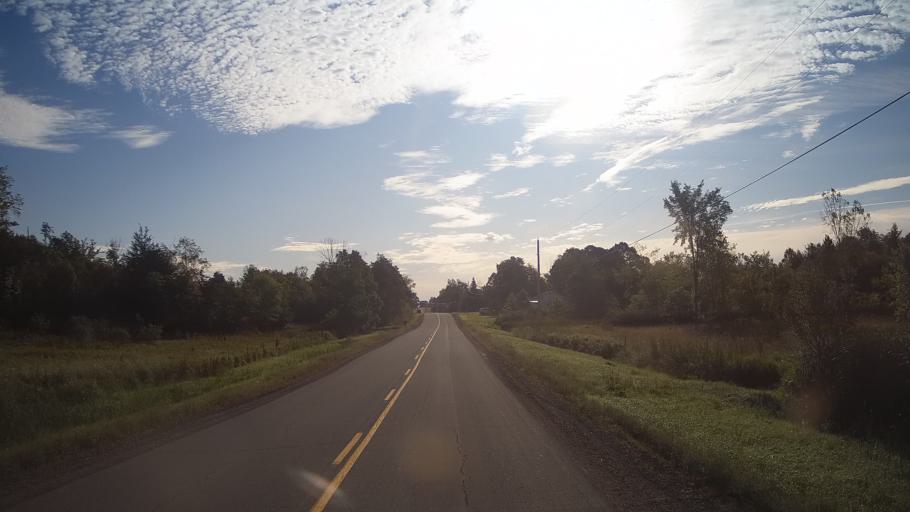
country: CA
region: Ontario
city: Gananoque
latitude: 44.4001
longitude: -76.1001
